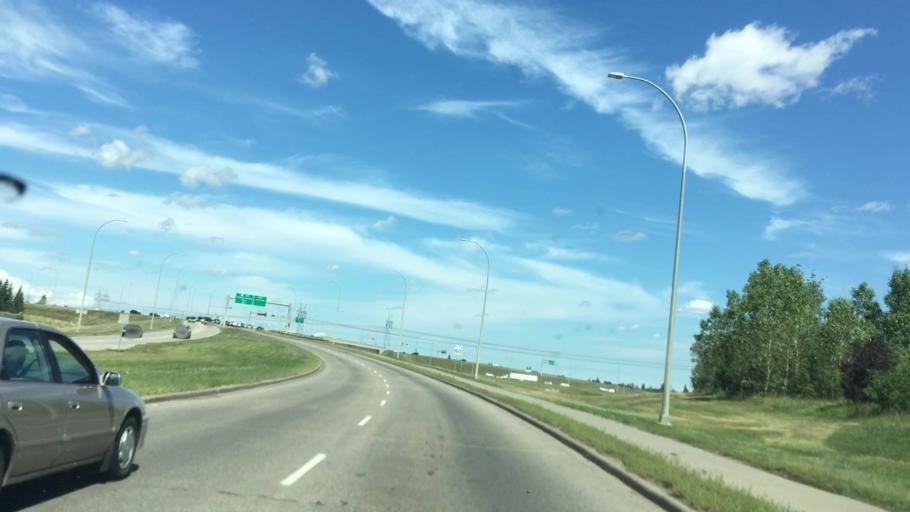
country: CA
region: Alberta
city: Beaumont
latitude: 53.4301
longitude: -113.5166
